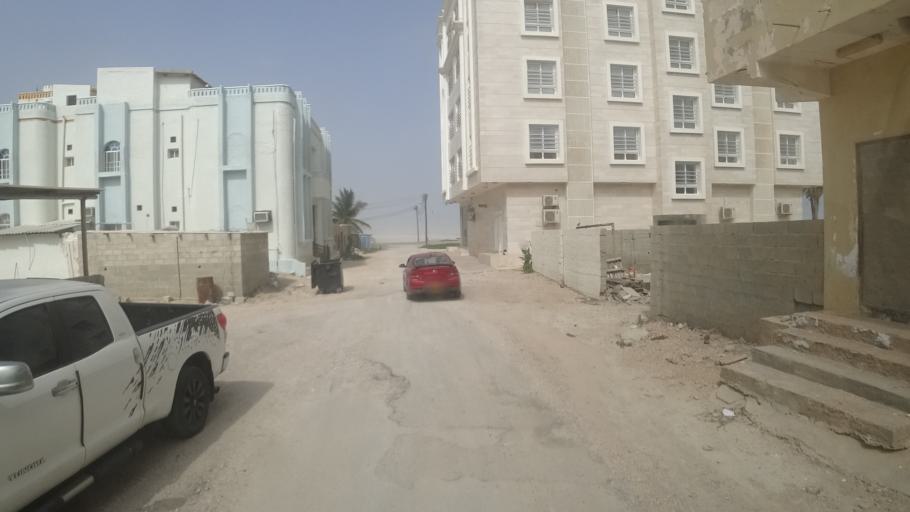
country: OM
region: Zufar
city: Salalah
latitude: 17.0097
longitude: 54.1623
